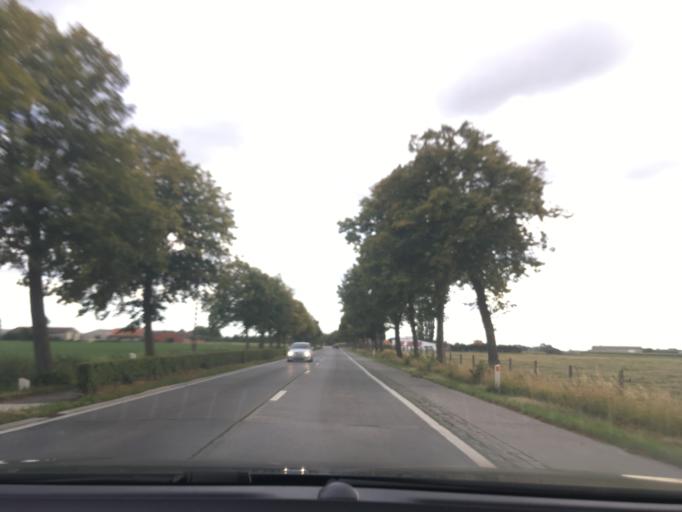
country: BE
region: Flanders
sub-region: Provincie West-Vlaanderen
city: Zonnebeke
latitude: 50.9050
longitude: 2.9426
